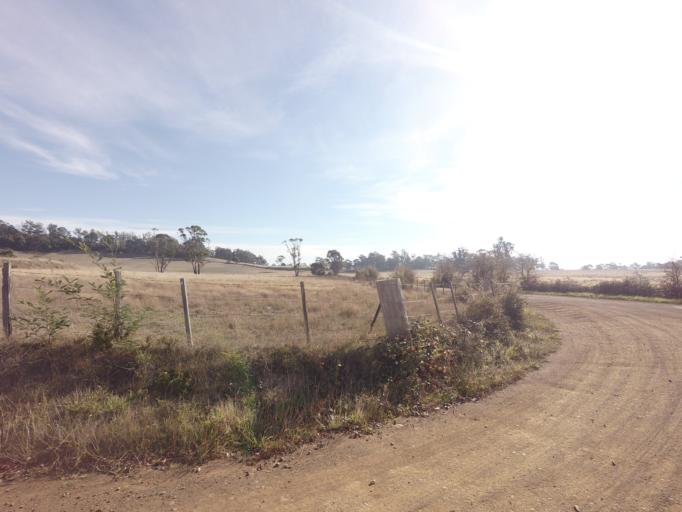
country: AU
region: Tasmania
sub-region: Sorell
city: Sorell
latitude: -42.4793
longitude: 147.4808
